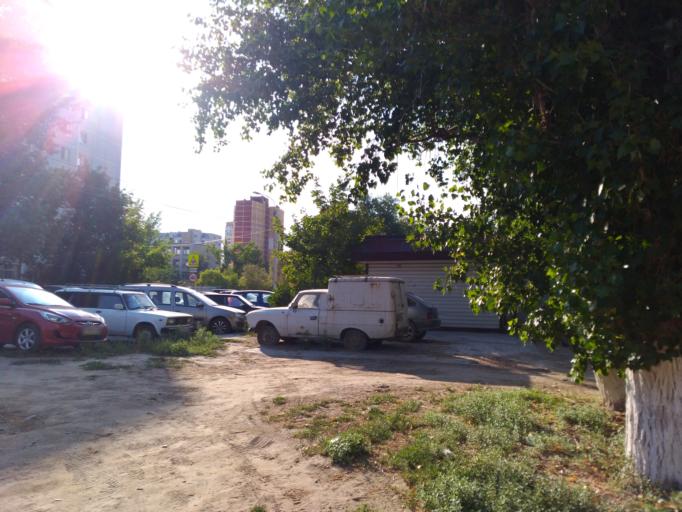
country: RU
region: Volgograd
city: Volgograd
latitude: 48.7199
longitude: 44.5152
